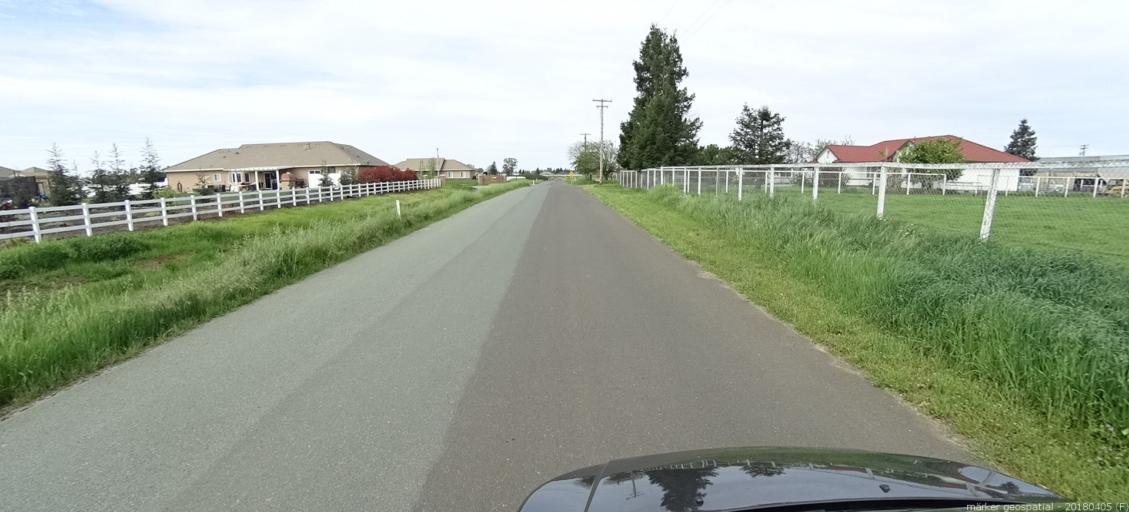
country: US
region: California
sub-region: Sacramento County
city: Galt
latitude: 38.2740
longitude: -121.3191
